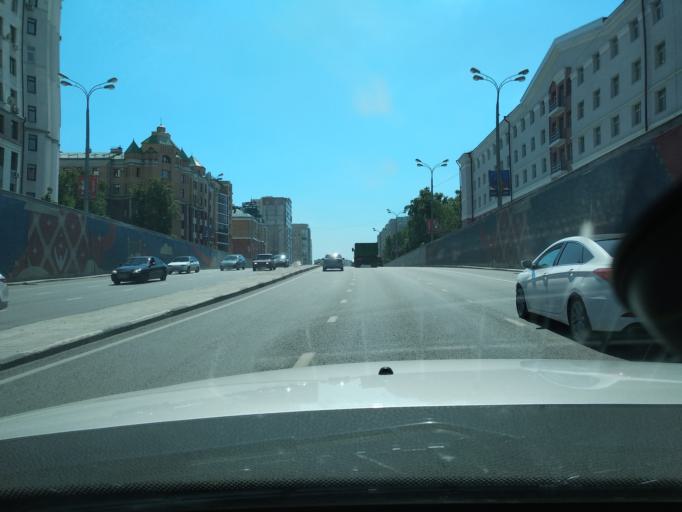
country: RU
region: Tatarstan
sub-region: Gorod Kazan'
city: Kazan
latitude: 55.7919
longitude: 49.1527
